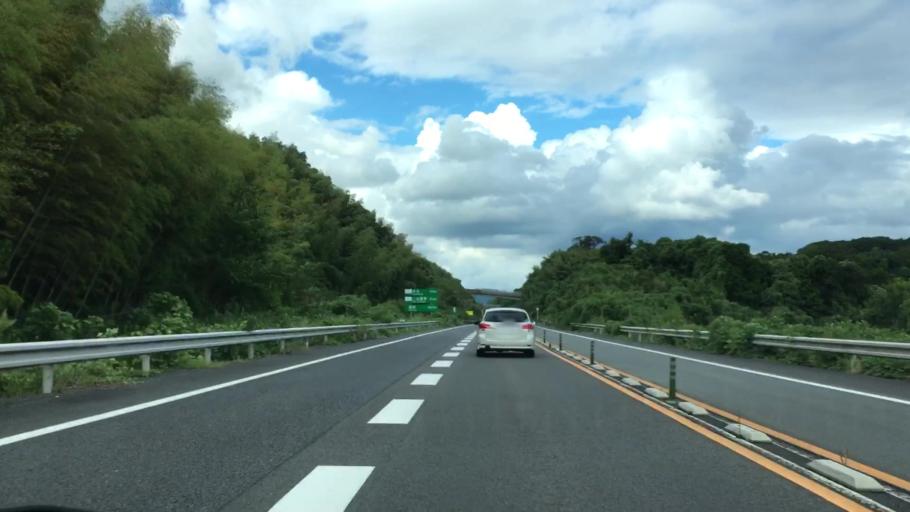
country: JP
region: Saga Prefecture
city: Karatsu
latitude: 33.4193
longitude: 130.0279
